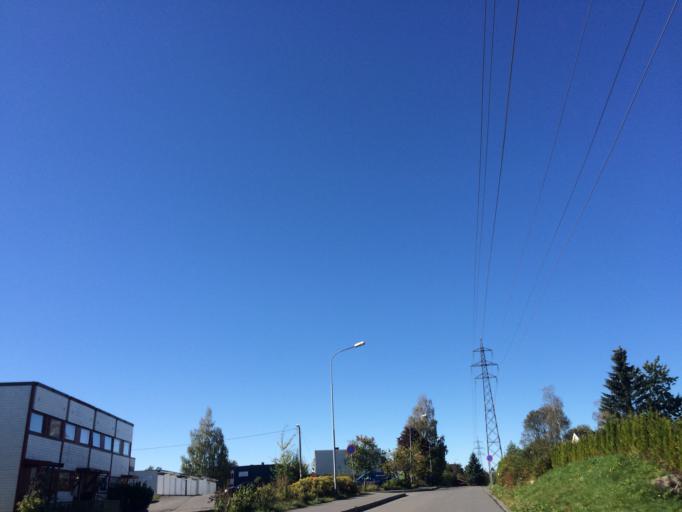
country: NO
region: Akershus
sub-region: Ski
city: Ski
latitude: 59.7155
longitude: 10.8175
